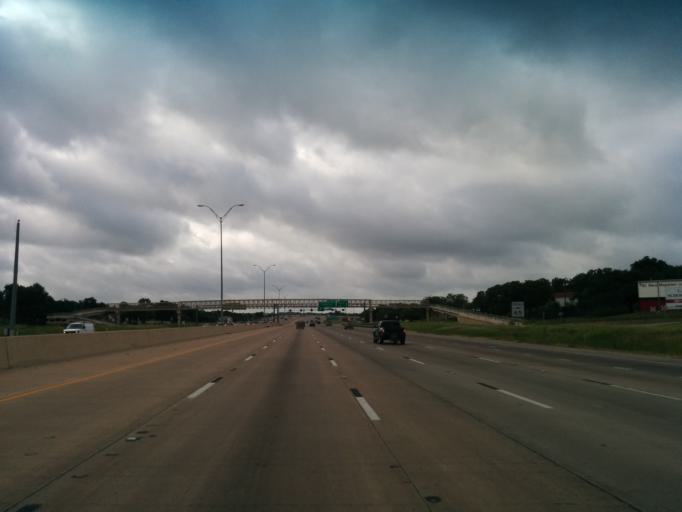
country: US
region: Texas
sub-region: Bexar County
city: Balcones Heights
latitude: 29.4788
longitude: -98.5227
